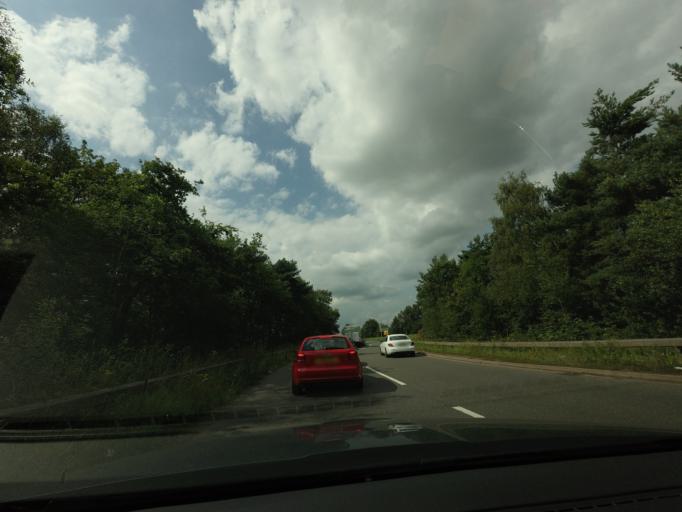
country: GB
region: England
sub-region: Staffordshire
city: Penkridge
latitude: 52.6886
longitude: -2.1045
